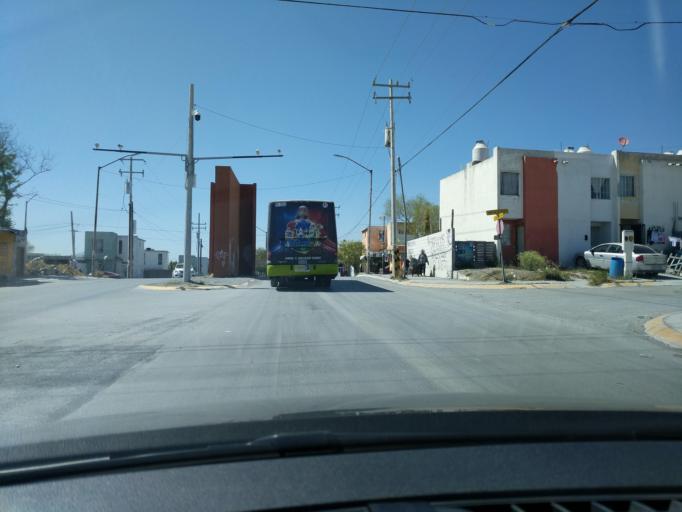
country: MX
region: Nuevo Leon
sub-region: Juarez
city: San Antonio
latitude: 25.6492
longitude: -100.0711
